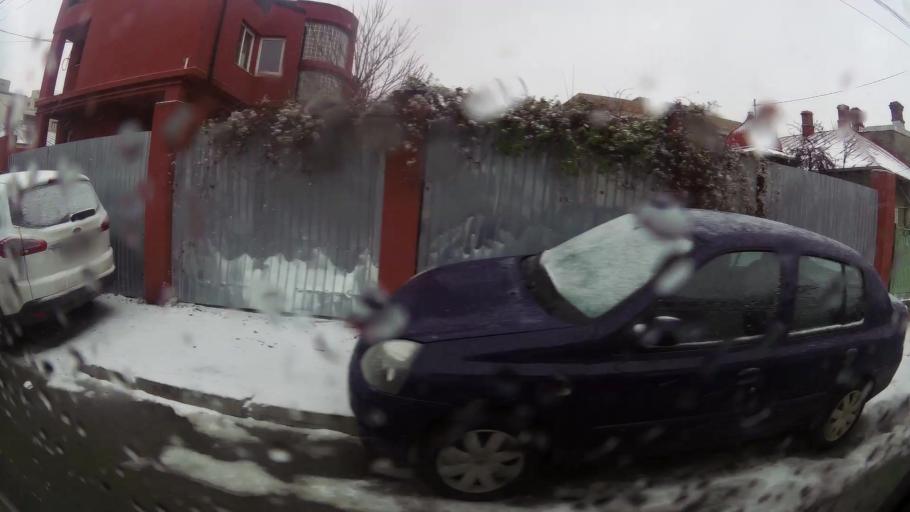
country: RO
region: Prahova
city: Ploiesti
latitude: 44.9474
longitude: 26.0066
